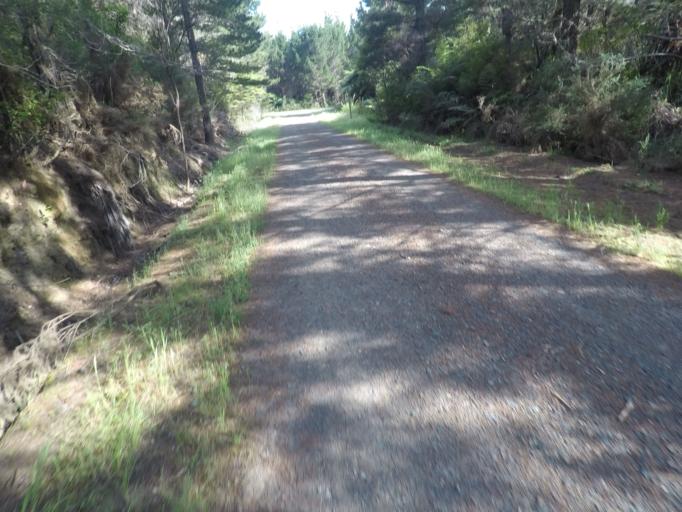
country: NZ
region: Auckland
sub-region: Auckland
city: Muriwai Beach
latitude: -36.7408
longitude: 174.5742
